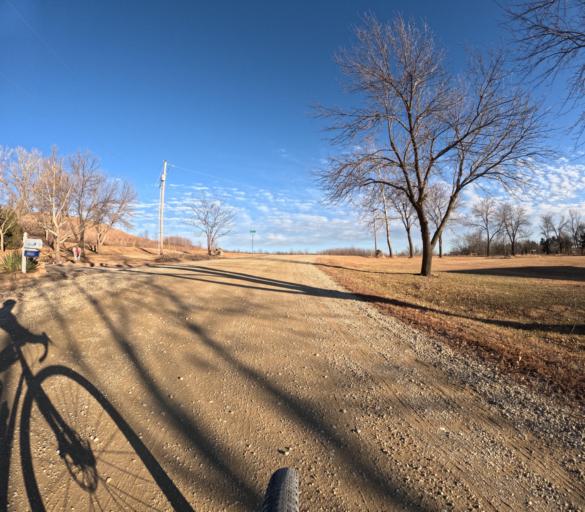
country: US
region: Kansas
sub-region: Riley County
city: Ogden
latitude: 39.2193
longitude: -96.6824
